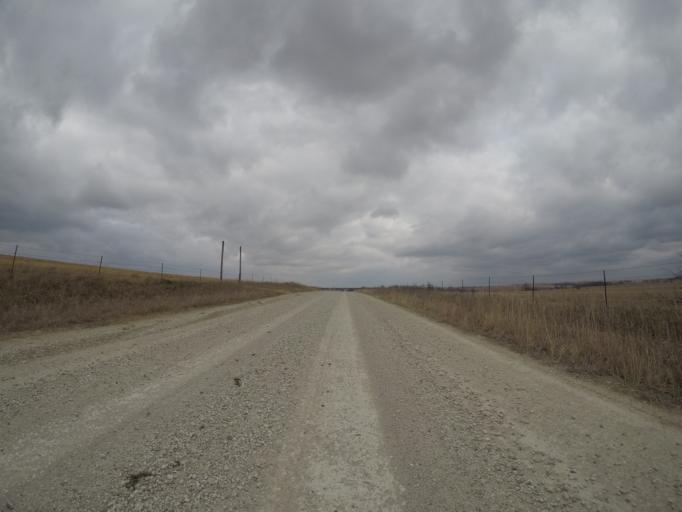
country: US
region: Kansas
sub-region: Morris County
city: Council Grove
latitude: 38.7271
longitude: -96.2796
